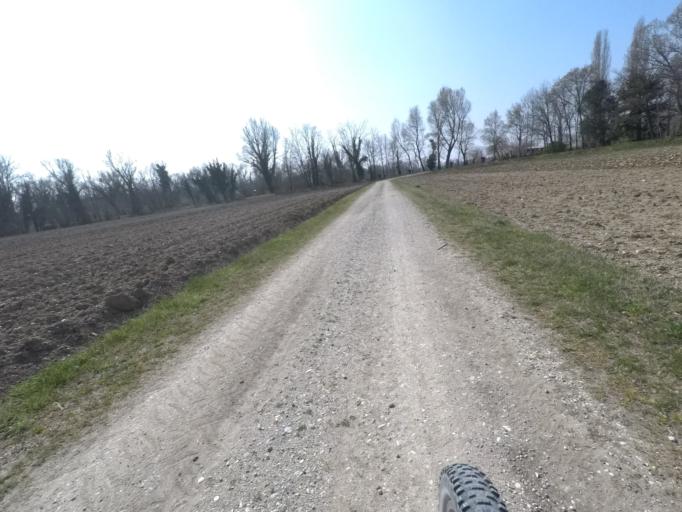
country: IT
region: Friuli Venezia Giulia
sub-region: Provincia di Udine
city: Remanzacco
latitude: 46.0603
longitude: 13.3254
